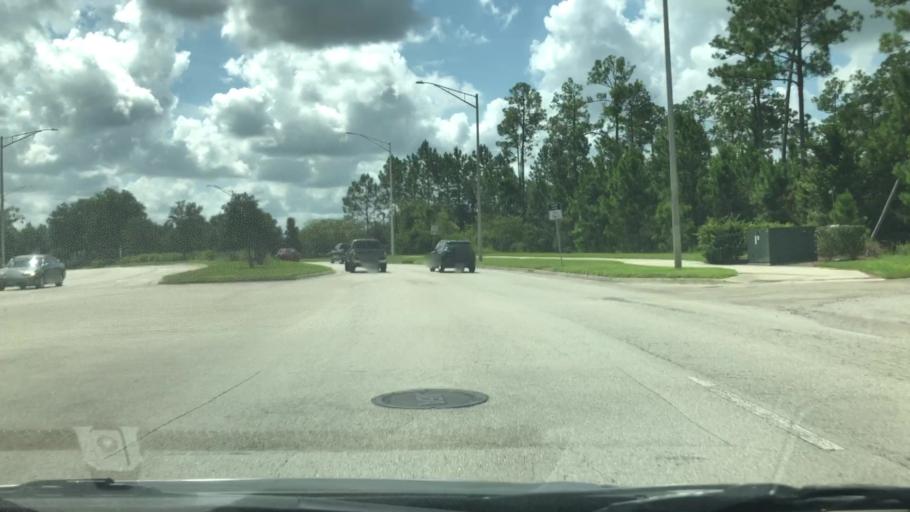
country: US
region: Florida
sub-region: Saint Johns County
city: Fruit Cove
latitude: 30.1306
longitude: -81.5431
